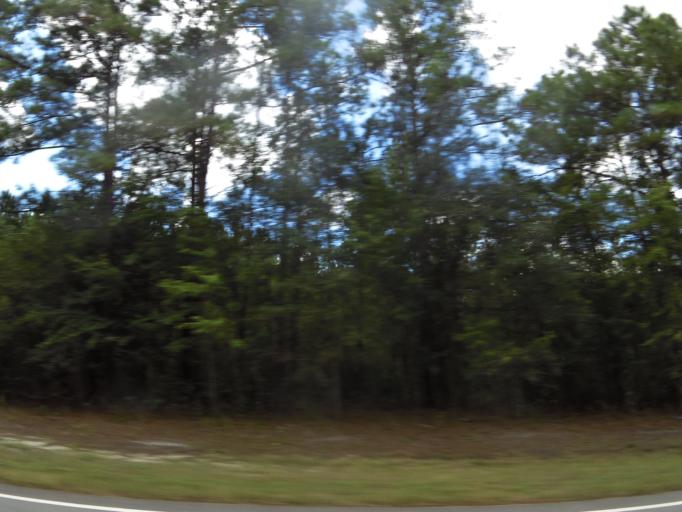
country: US
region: Georgia
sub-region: Brantley County
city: Nahunta
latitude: 31.0543
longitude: -82.0164
